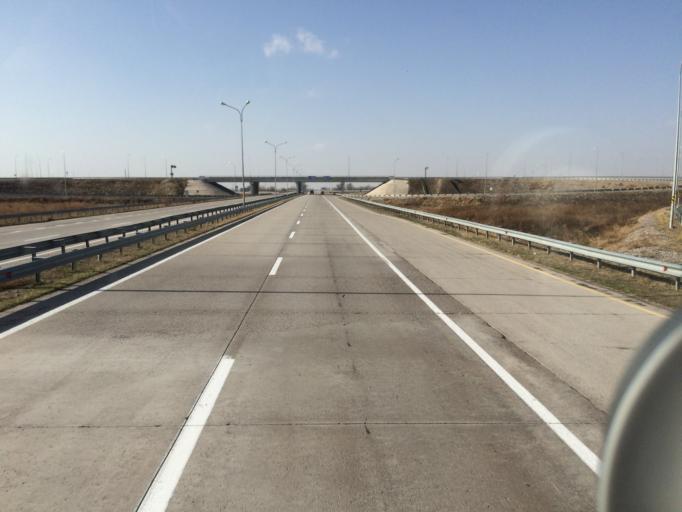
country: KZ
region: Zhambyl
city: Oytal
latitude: 42.9283
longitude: 73.2458
